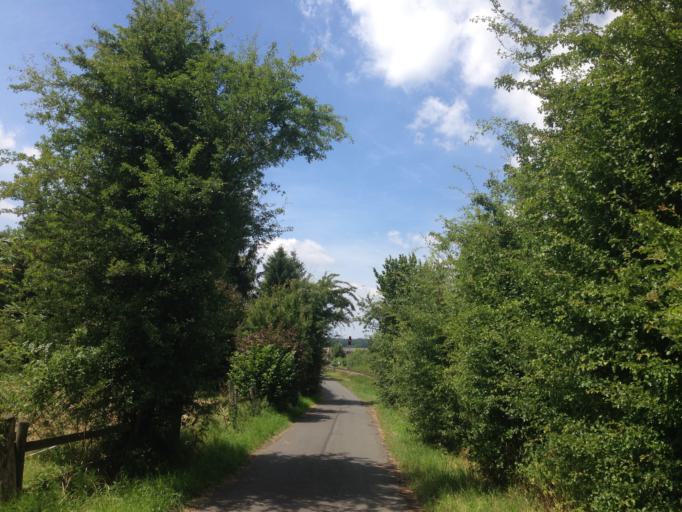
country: DE
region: Hesse
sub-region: Regierungsbezirk Giessen
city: Reiskirchen
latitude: 50.5986
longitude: 8.8397
